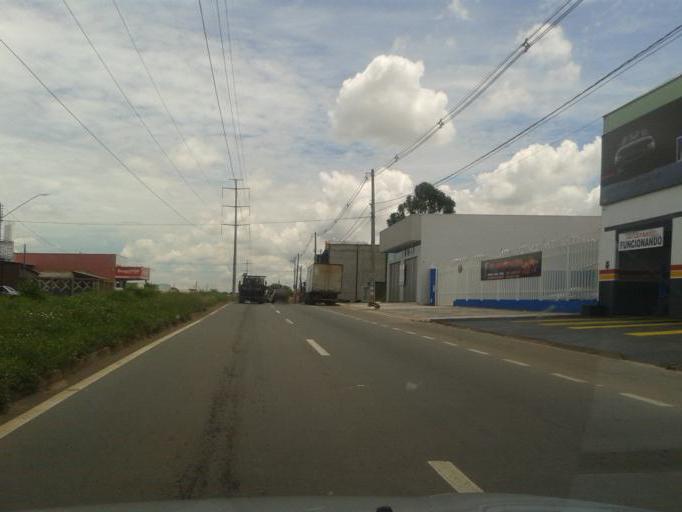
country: BR
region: Goias
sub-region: Aparecida De Goiania
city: Aparecida de Goiania
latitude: -16.7687
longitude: -49.3214
